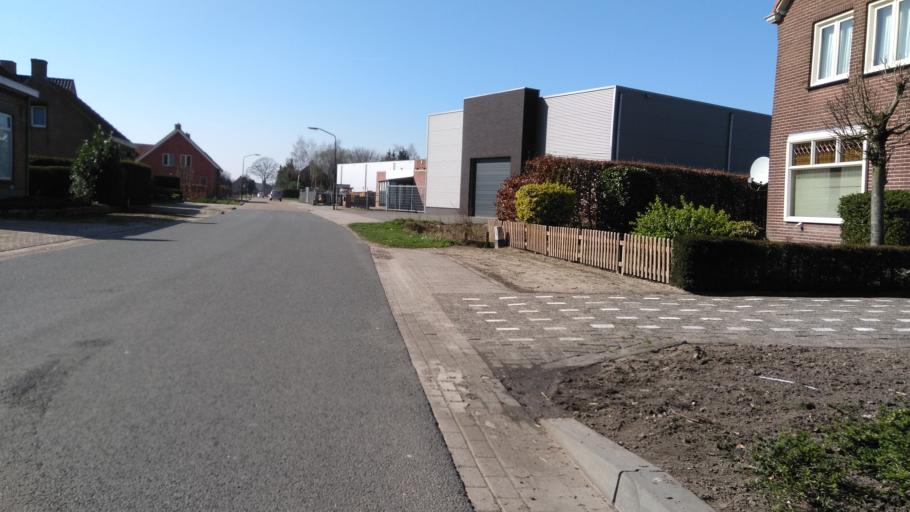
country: NL
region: North Brabant
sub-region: Gemeente Baarle-Nassau
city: Baarle-Nassau
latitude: 51.4417
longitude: 4.9427
